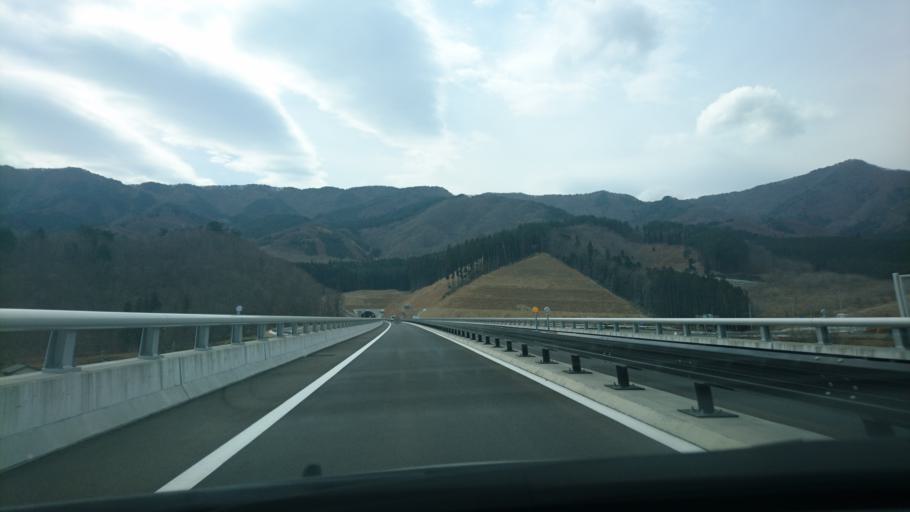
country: JP
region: Iwate
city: Kamaishi
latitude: 39.1928
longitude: 141.8523
